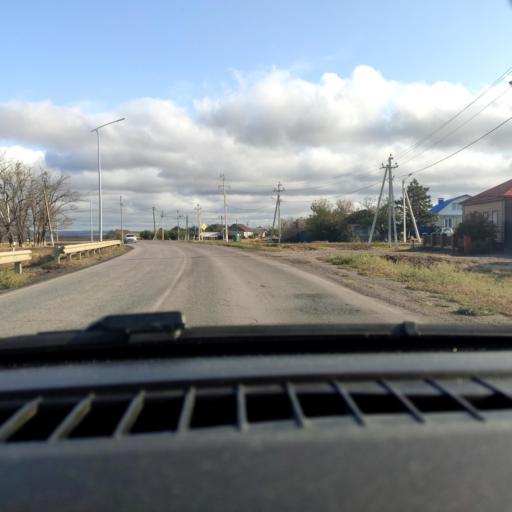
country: RU
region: Belgorod
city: Ilovka
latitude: 50.7331
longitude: 38.6990
